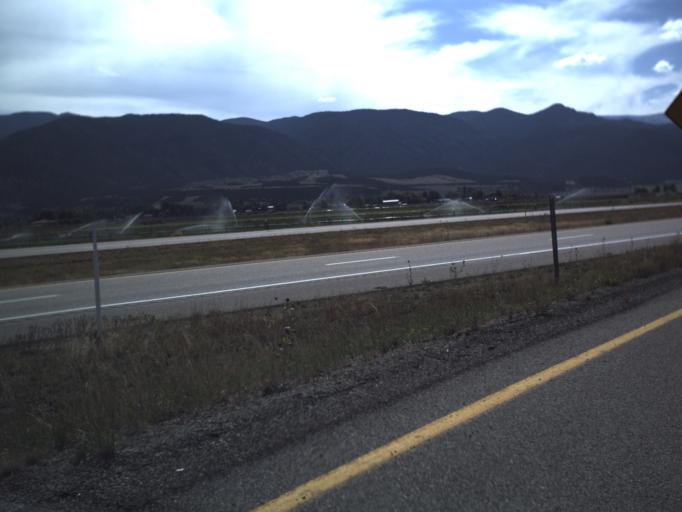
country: US
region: Utah
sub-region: Iron County
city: Parowan
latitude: 37.9070
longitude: -112.7792
